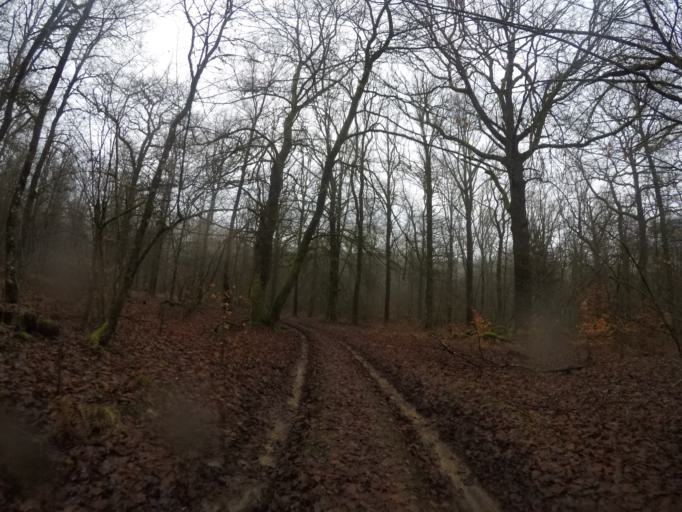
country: BE
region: Wallonia
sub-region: Province du Luxembourg
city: Leglise
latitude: 49.8135
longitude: 5.6030
